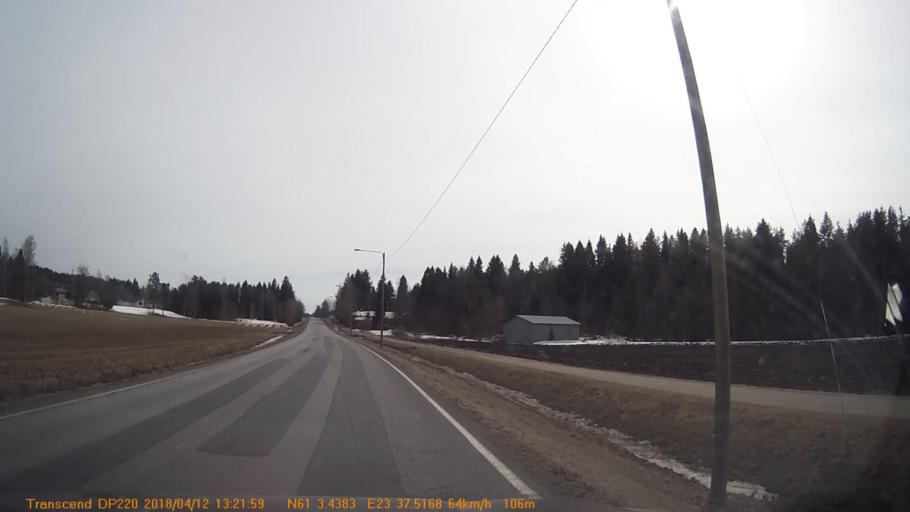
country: FI
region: Pirkanmaa
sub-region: Etelae-Pirkanmaa
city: Urjala
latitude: 61.0561
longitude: 23.6260
